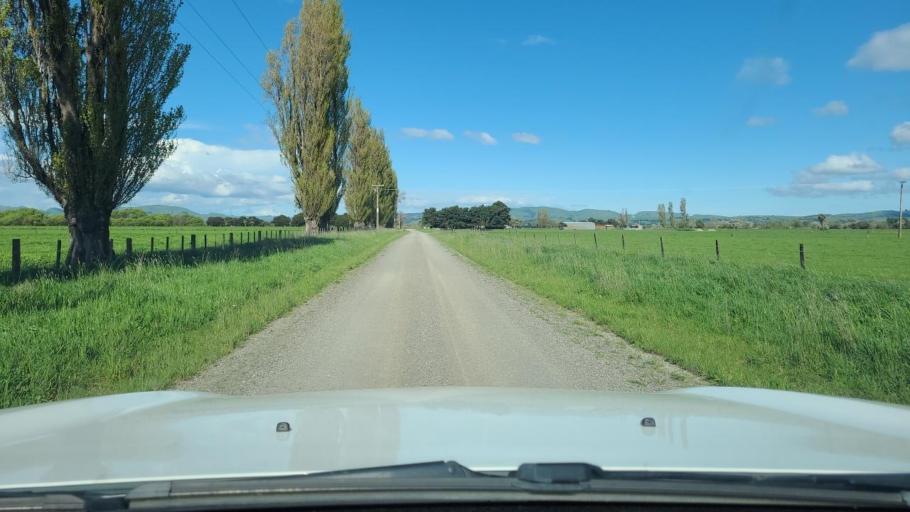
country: NZ
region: Wellington
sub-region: South Wairarapa District
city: Waipawa
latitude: -41.2096
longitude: 175.3904
